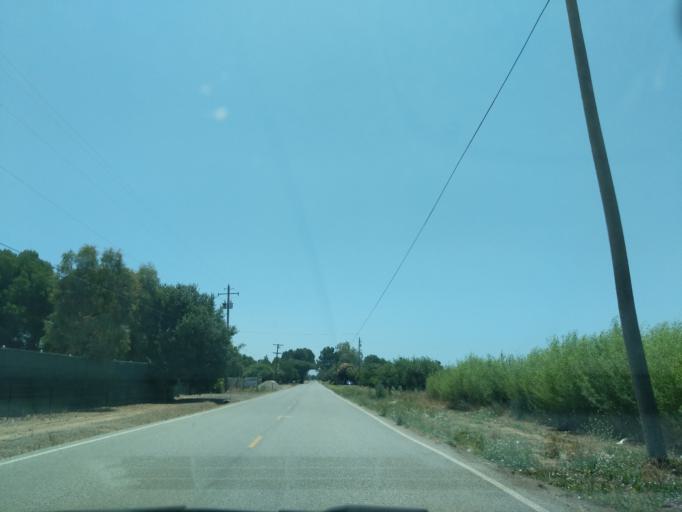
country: US
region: California
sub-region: Santa Clara County
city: San Martin
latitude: 37.0998
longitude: -121.6146
